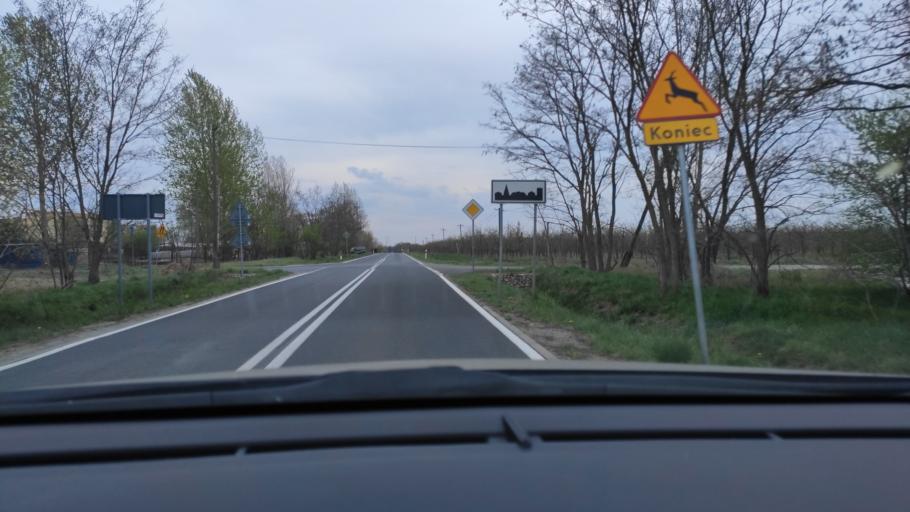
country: PL
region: Masovian Voivodeship
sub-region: Powiat zwolenski
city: Zwolen
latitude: 51.3648
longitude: 21.5644
